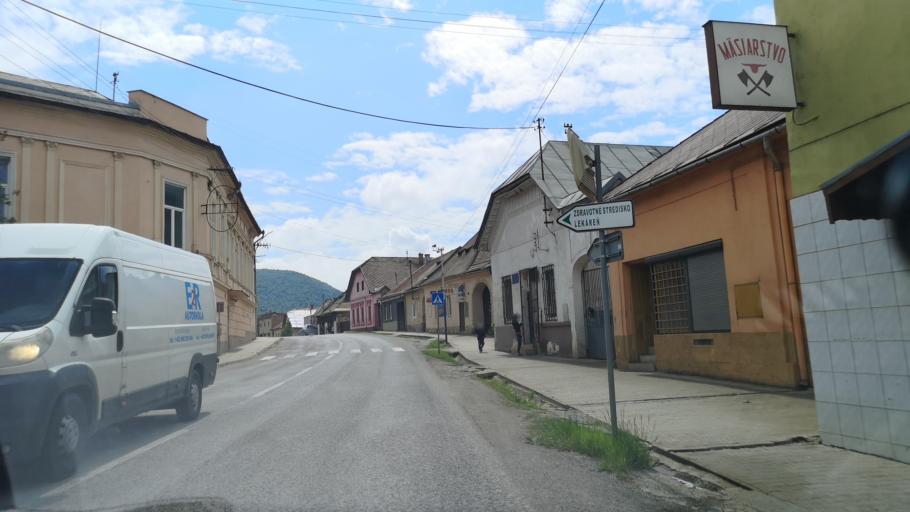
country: SK
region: Banskobystricky
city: Revuca
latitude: 48.6288
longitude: 20.2369
